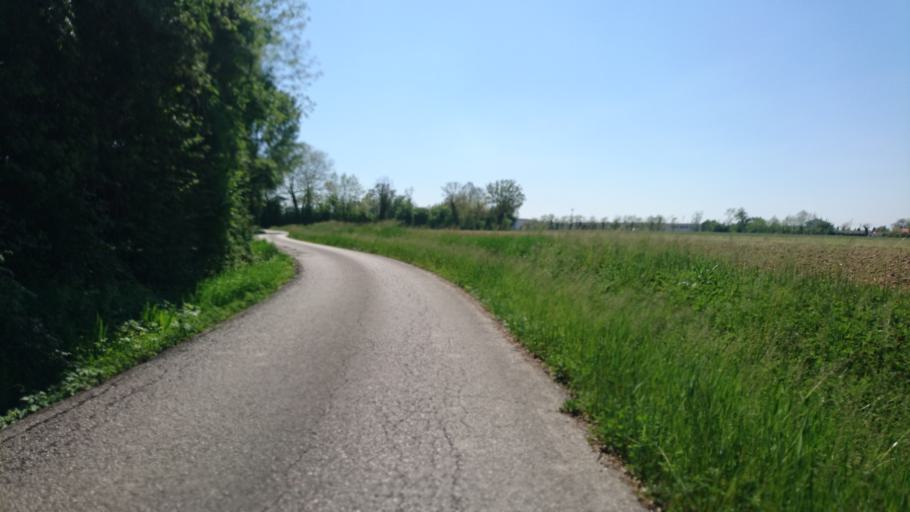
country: IT
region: Veneto
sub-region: Provincia di Treviso
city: Conscio
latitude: 45.6165
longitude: 12.2746
